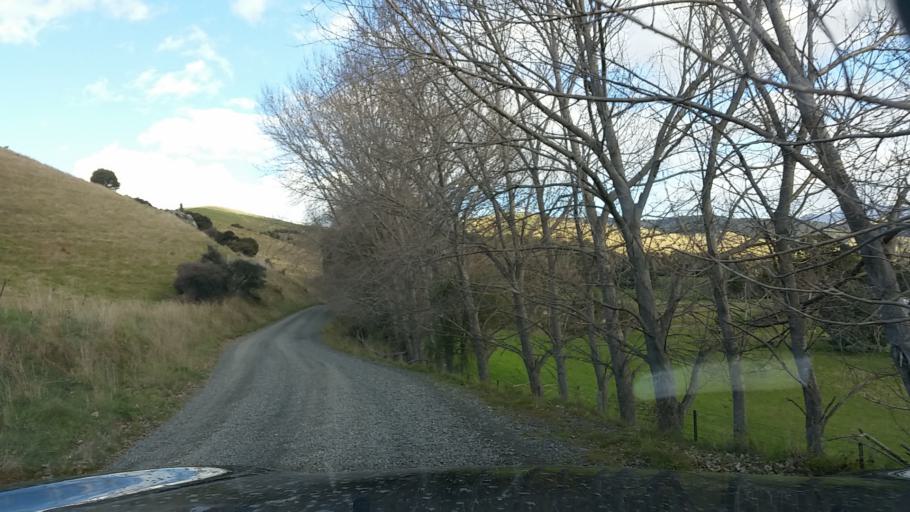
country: NZ
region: Marlborough
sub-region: Marlborough District
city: Blenheim
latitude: -41.7663
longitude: 173.8576
